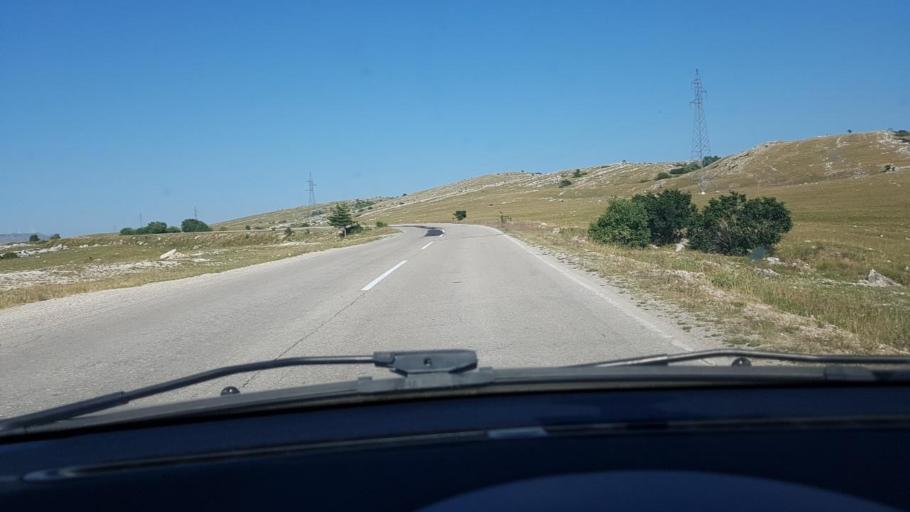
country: BA
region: Federation of Bosnia and Herzegovina
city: Tomislavgrad
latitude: 43.8042
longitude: 17.2665
